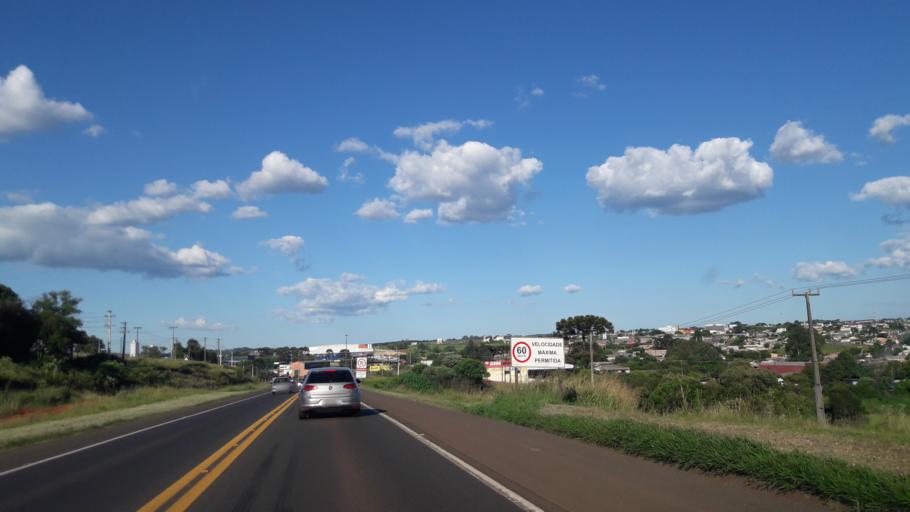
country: BR
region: Parana
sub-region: Guarapuava
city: Guarapuava
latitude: -25.3691
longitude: -51.4956
